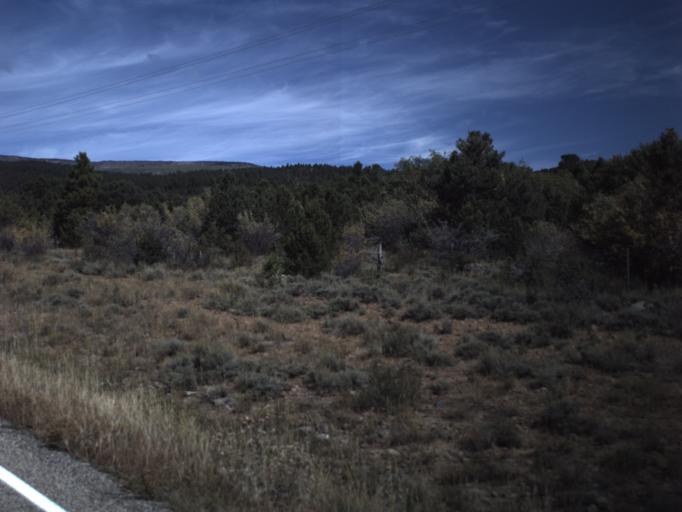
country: US
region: Utah
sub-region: Wayne County
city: Loa
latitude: 37.9745
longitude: -111.4311
